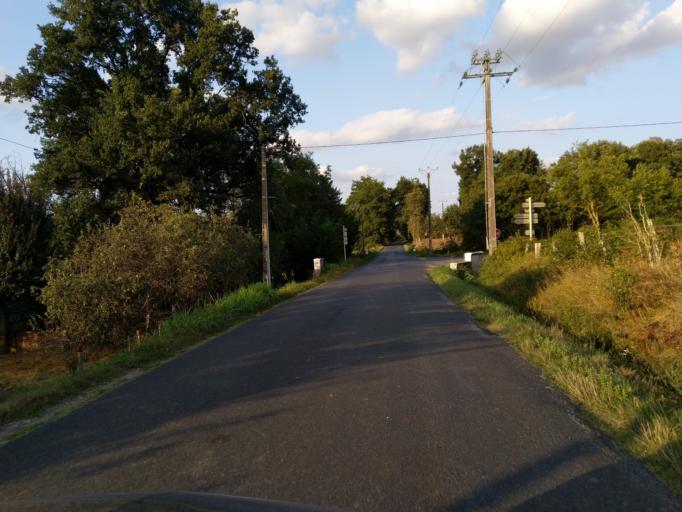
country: FR
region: Midi-Pyrenees
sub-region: Departement du Tarn
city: Frejairolles
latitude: 43.8364
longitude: 2.2122
